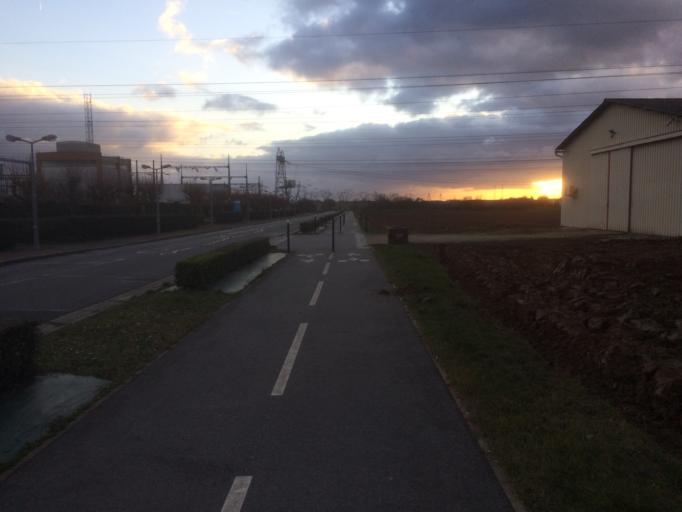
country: FR
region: Ile-de-France
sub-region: Departement de l'Essonne
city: Villejust
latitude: 48.6782
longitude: 2.2299
